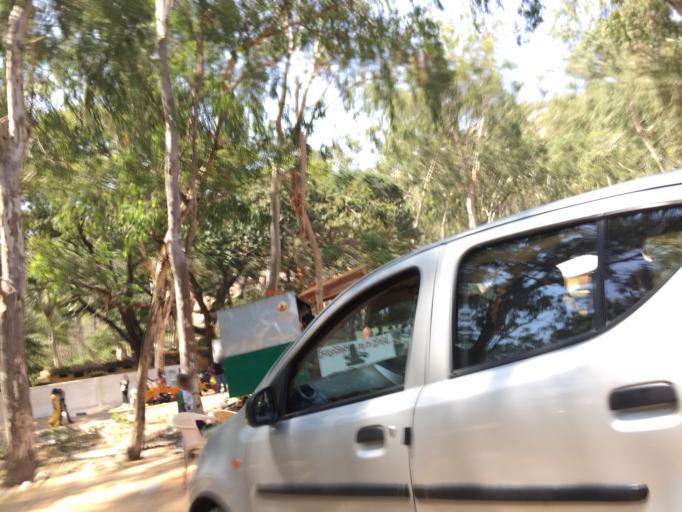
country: IN
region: Karnataka
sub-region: Kolar
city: Kolar
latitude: 13.1414
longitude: 78.1051
